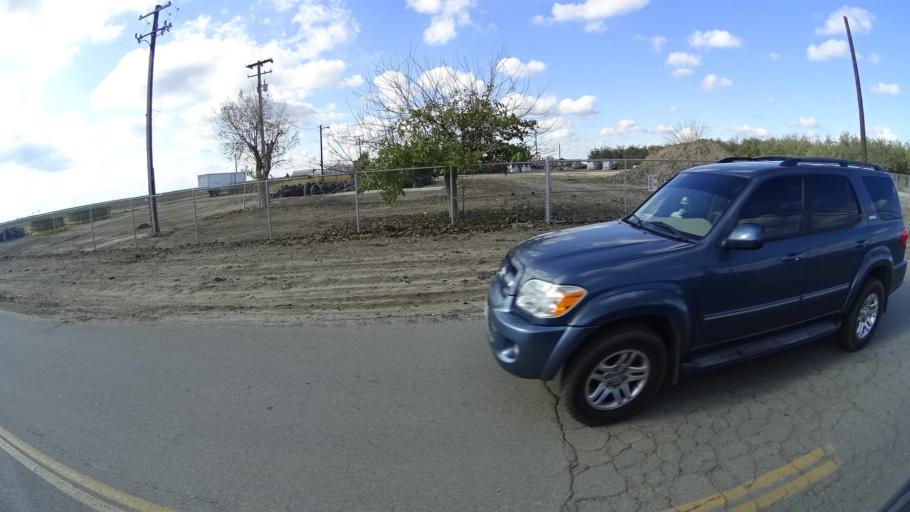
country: US
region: California
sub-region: Kern County
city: McFarland
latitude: 35.6857
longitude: -119.2409
